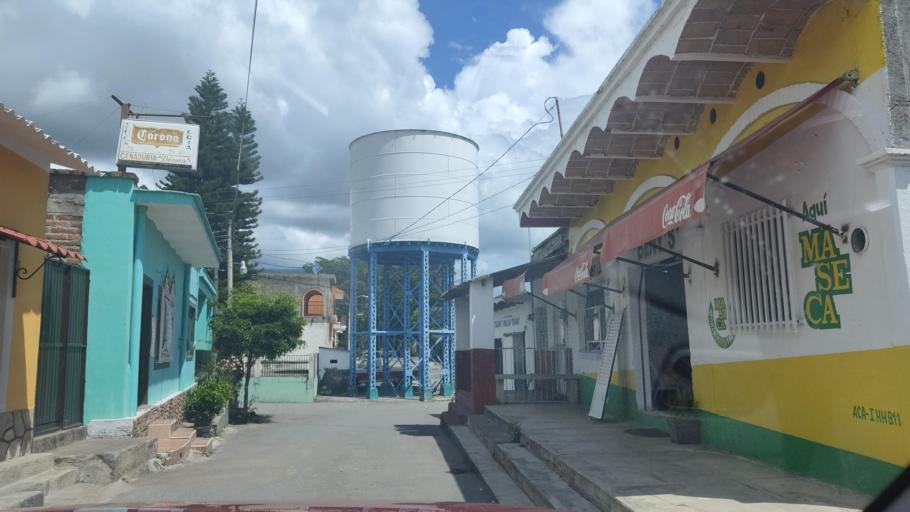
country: MX
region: Nayarit
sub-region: Ahuacatlan
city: Ahuacatlan
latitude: 21.1196
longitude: -104.6210
